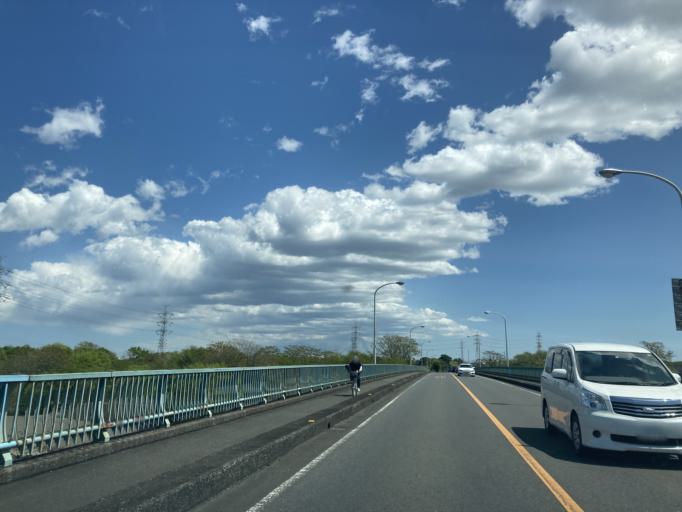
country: JP
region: Saitama
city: Sayama
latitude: 35.8754
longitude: 139.4111
